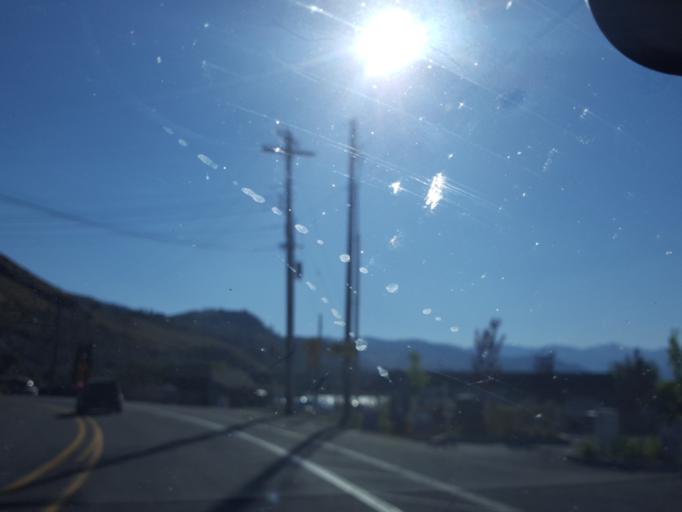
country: US
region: Washington
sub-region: Chelan County
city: Chelan
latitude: 47.8360
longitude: -120.0368
